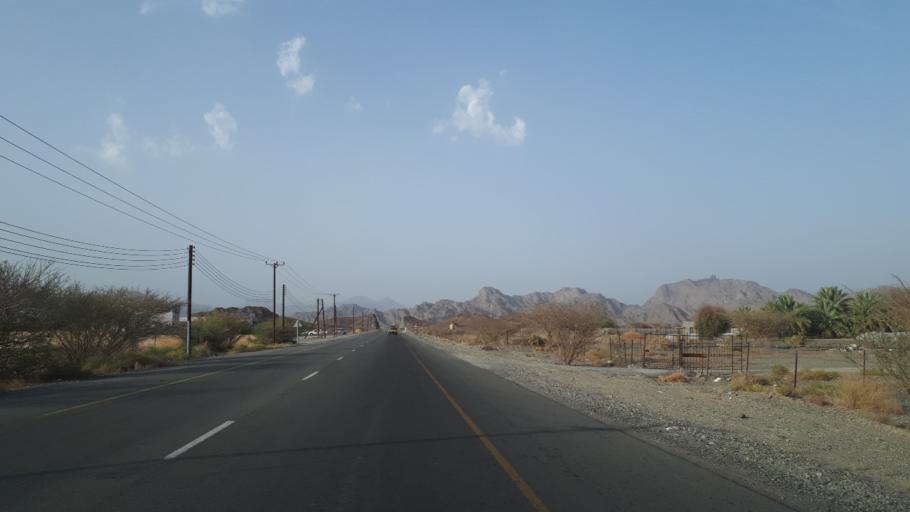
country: OM
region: Az Zahirah
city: Yanqul
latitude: 23.4416
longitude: 56.7826
